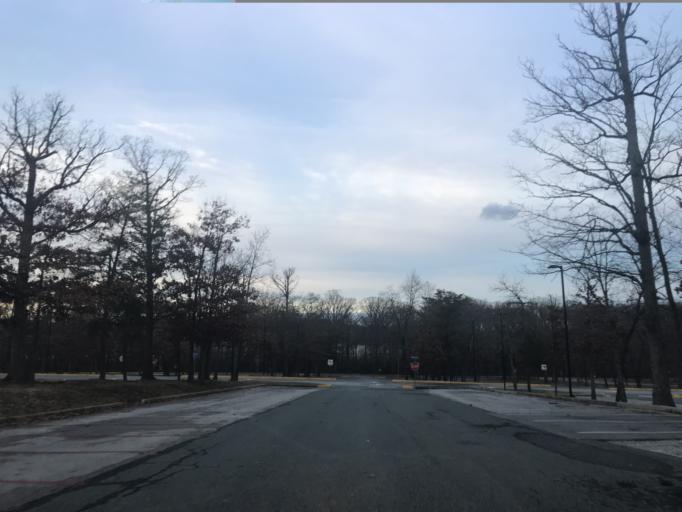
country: US
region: Maryland
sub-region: Baltimore County
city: Rossville
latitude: 39.3548
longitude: -76.4826
